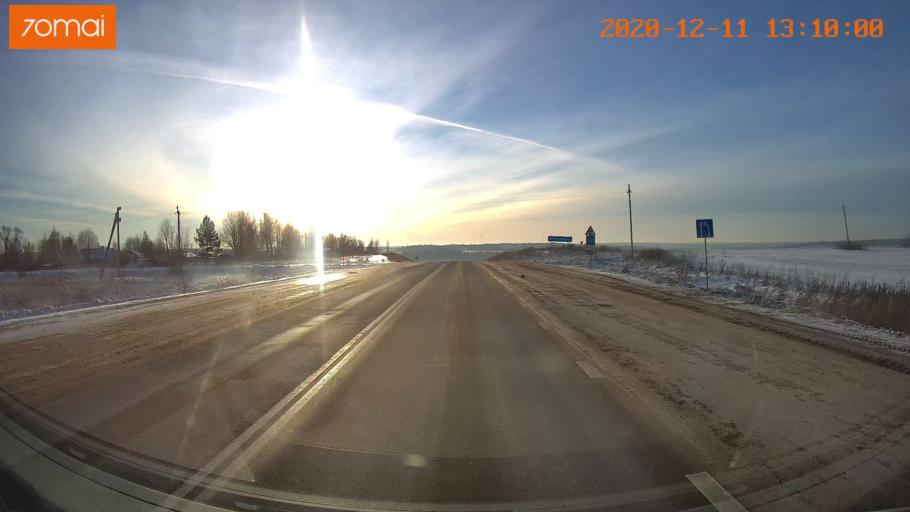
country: RU
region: Kostroma
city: Susanino
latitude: 58.1794
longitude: 41.6417
